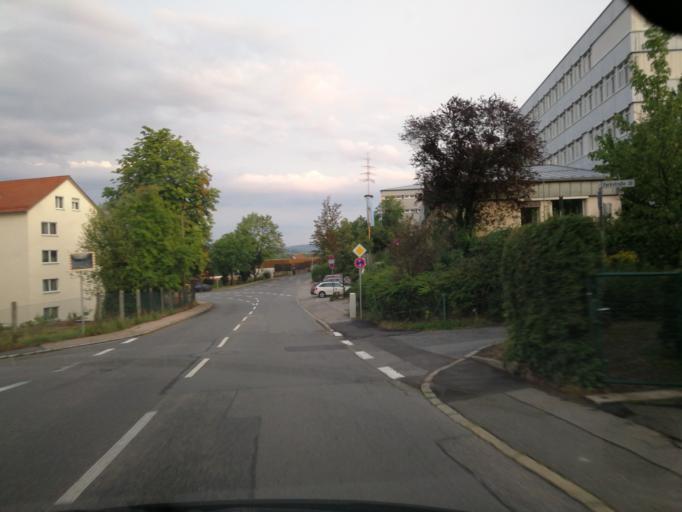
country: DE
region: Bavaria
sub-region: Upper Palatinate
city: Cham
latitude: 49.2258
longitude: 12.6680
